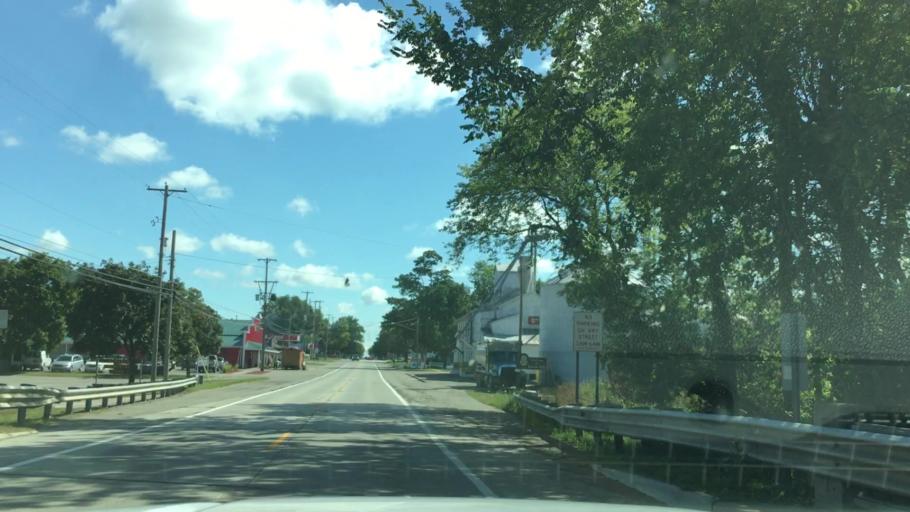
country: US
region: Michigan
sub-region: Montcalm County
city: Carson City
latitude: 43.1771
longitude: -84.8566
